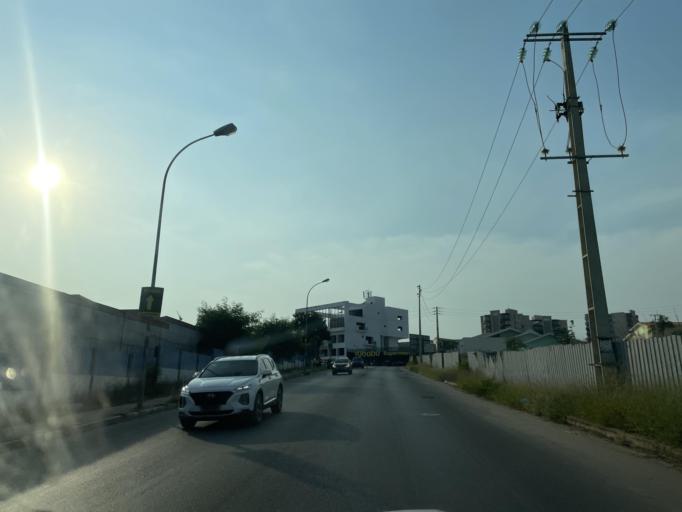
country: AO
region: Luanda
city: Luanda
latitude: -8.9231
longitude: 13.1969
